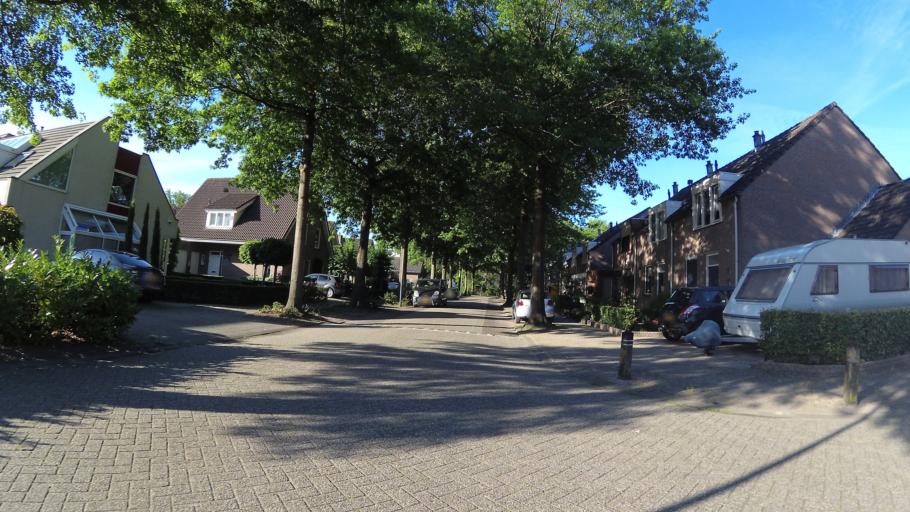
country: NL
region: North Brabant
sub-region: Gemeente Waalwijk
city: Waalwijk
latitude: 51.6537
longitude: 5.0375
